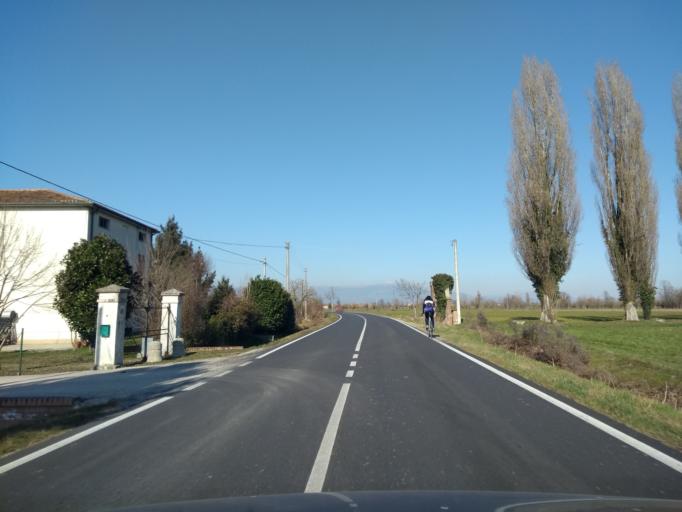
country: IT
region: Veneto
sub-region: Provincia di Vicenza
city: Bolzano Vicentino
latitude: 45.6015
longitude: 11.6440
